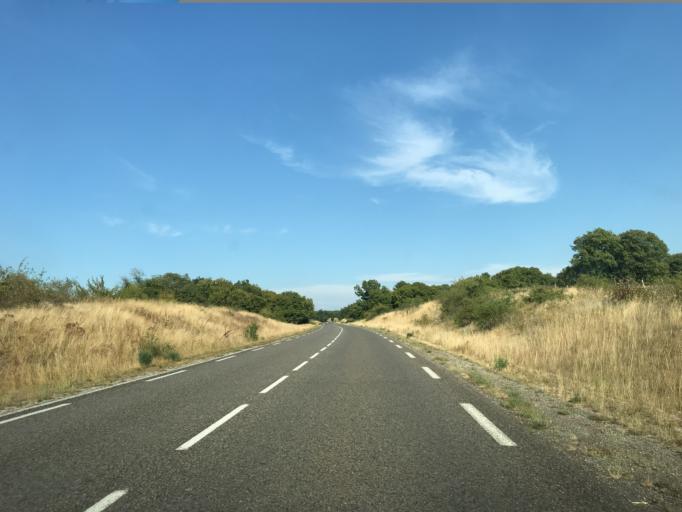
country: FR
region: Midi-Pyrenees
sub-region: Departement du Lot
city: Gramat
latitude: 44.6780
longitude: 1.6390
